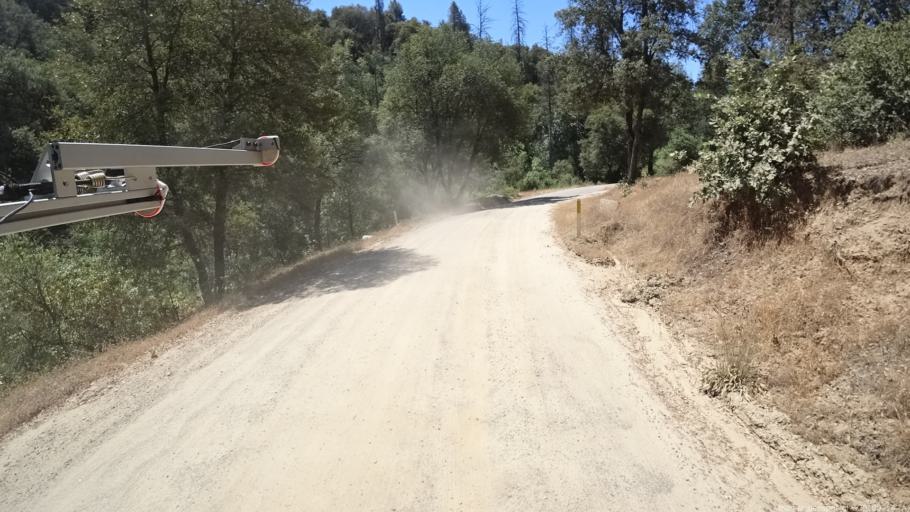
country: US
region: California
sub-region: Madera County
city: Ahwahnee
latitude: 37.3918
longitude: -119.6892
